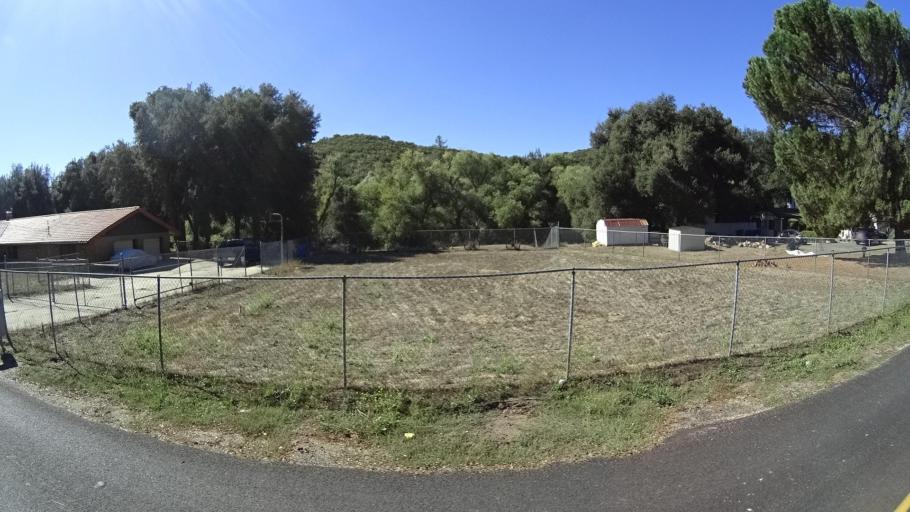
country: US
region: California
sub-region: San Diego County
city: Descanso
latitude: 32.8636
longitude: -116.6202
